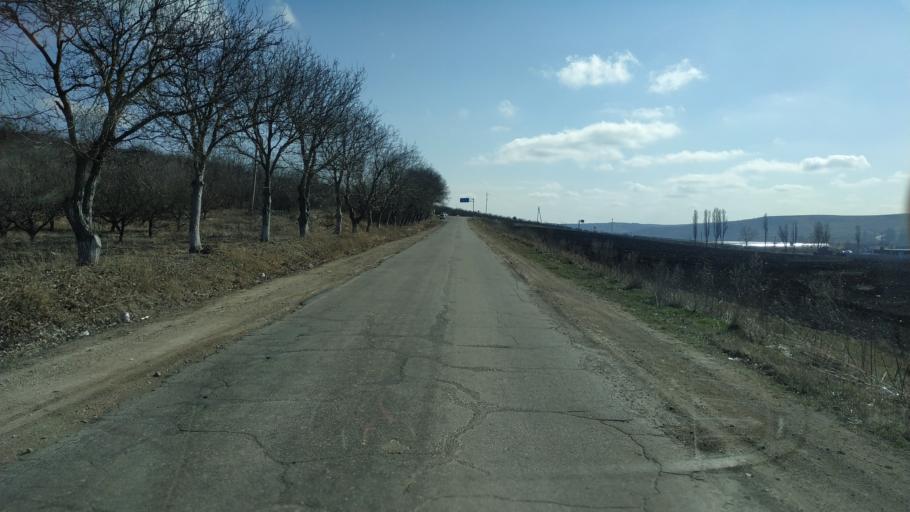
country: MD
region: Laloveni
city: Ialoveni
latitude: 46.9204
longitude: 28.6889
